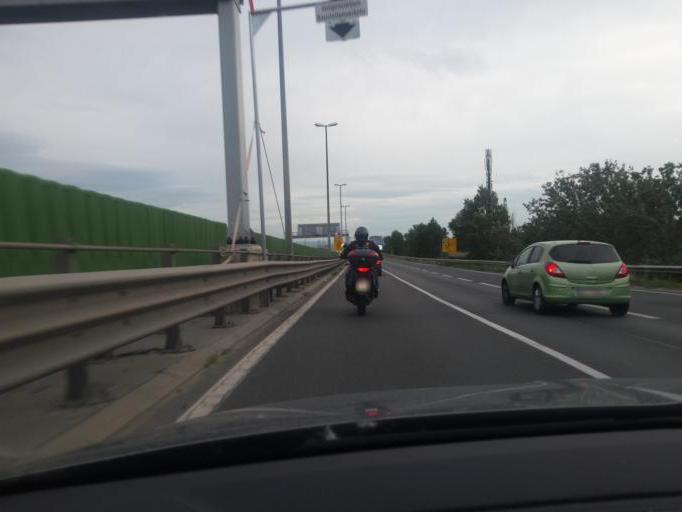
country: AT
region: Vienna
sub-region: Wien Stadt
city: Vienna
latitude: 48.2121
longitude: 16.4441
